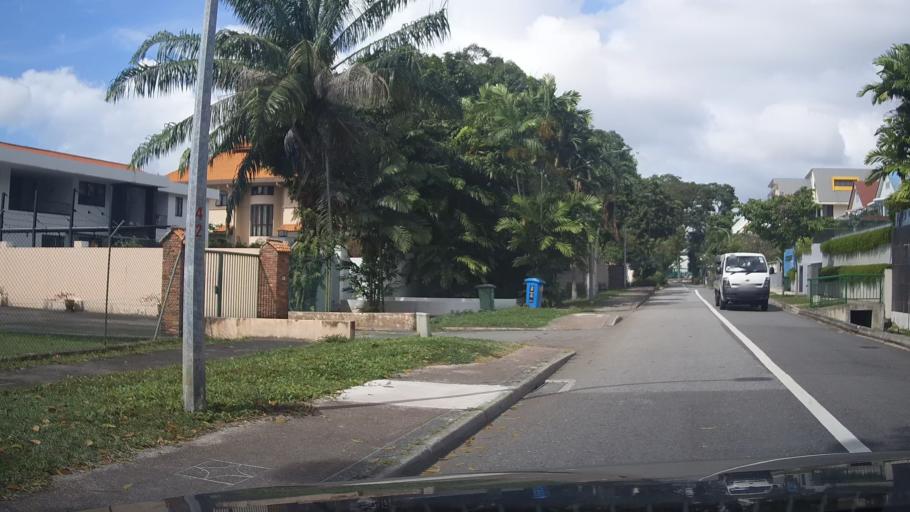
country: SG
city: Singapore
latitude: 1.3042
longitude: 103.8874
